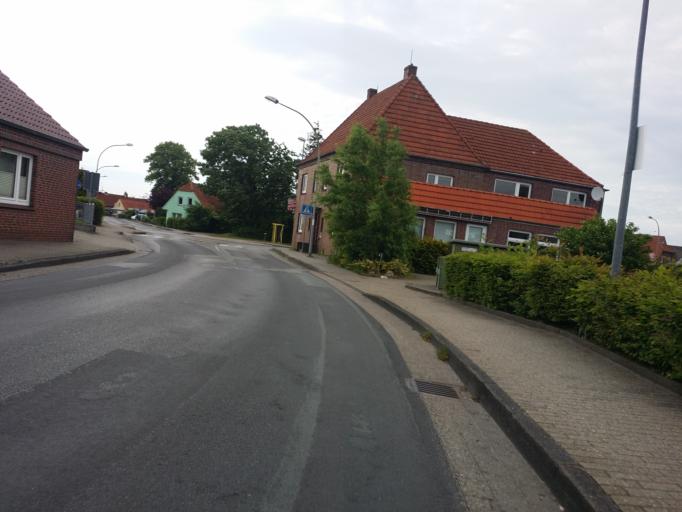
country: DE
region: Lower Saxony
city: Wittmund
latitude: 53.5779
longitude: 7.7801
